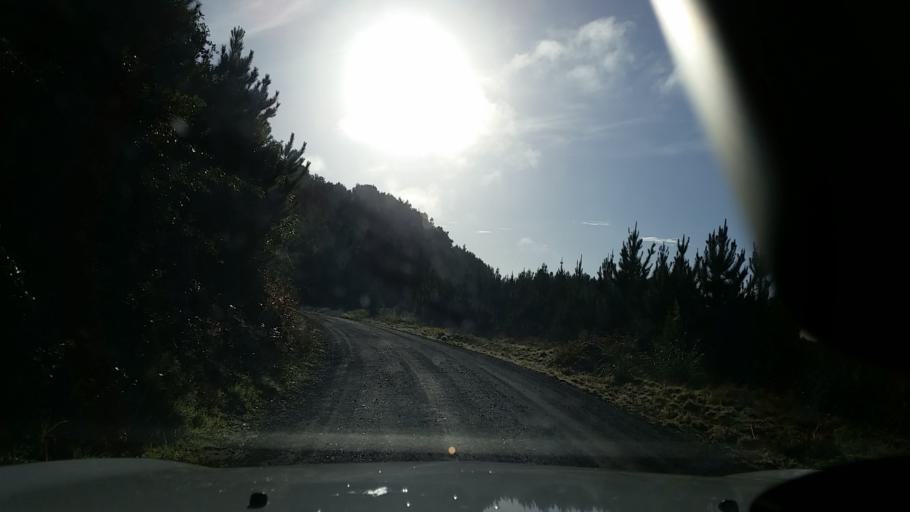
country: NZ
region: Bay of Plenty
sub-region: Kawerau District
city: Kawerau
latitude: -38.0327
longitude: 176.5530
